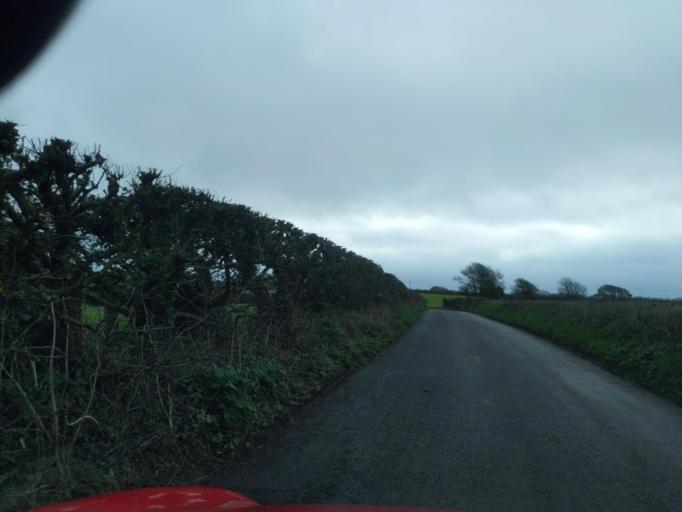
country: GB
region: England
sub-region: Devon
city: Wembury
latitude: 50.3304
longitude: -4.0944
